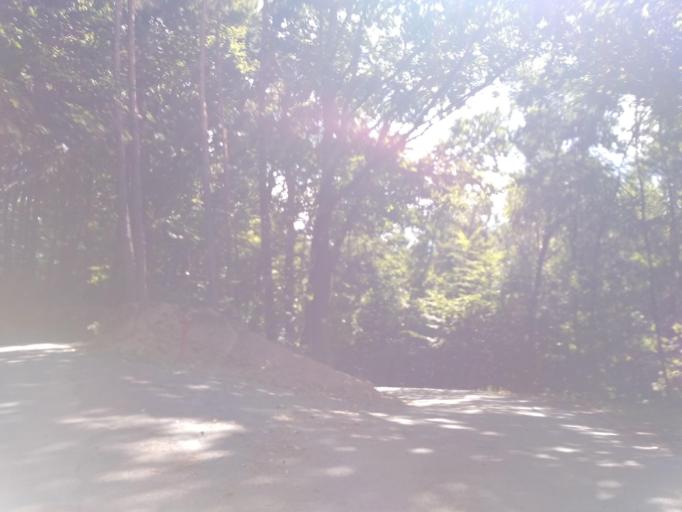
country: PL
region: Subcarpathian Voivodeship
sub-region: Powiat strzyzowski
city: Polomia
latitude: 49.9159
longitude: 21.8846
